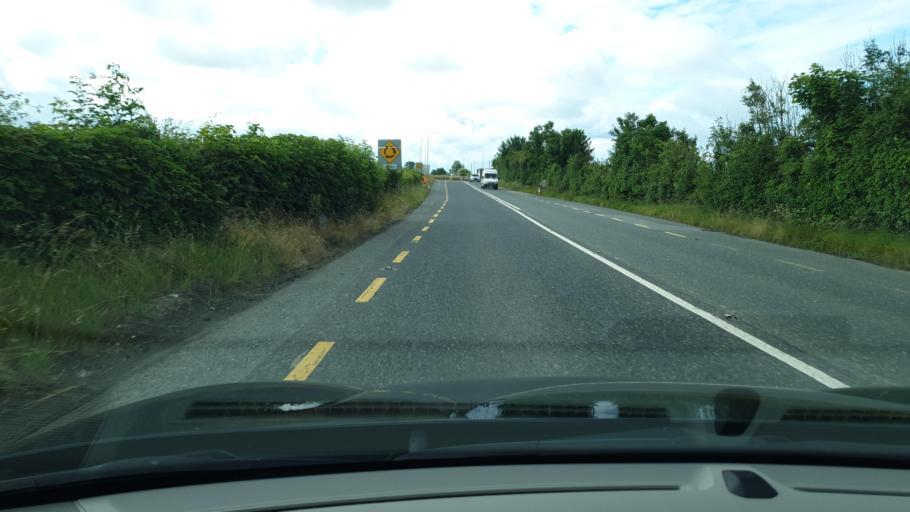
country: IE
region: Leinster
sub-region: Fingal County
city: Blanchardstown
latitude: 53.4474
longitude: -6.3429
